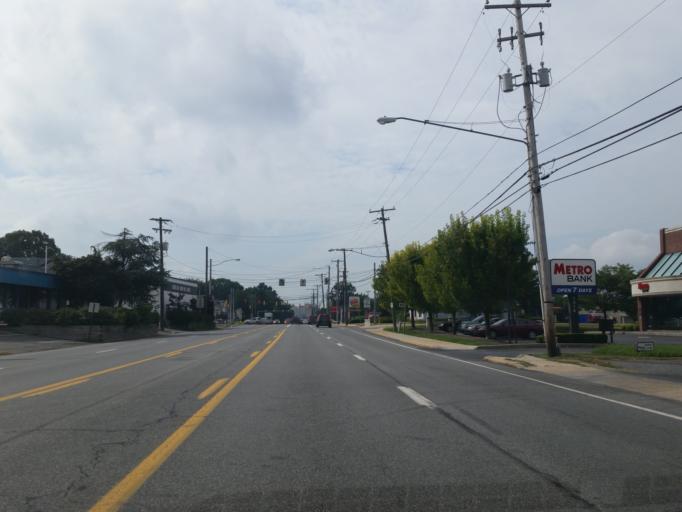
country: US
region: Pennsylvania
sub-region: Lancaster County
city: Lancaster
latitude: 40.0625
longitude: -76.3066
